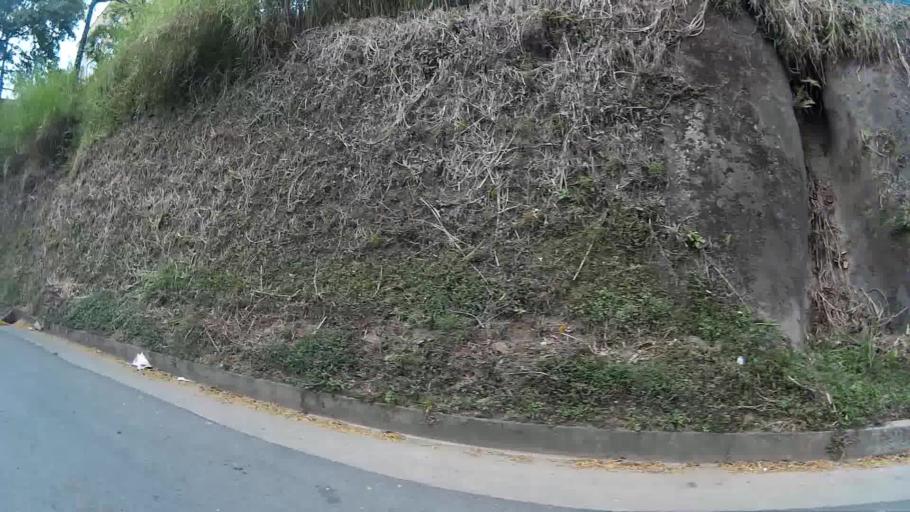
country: CO
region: Risaralda
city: Pereira
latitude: 4.8142
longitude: -75.7606
